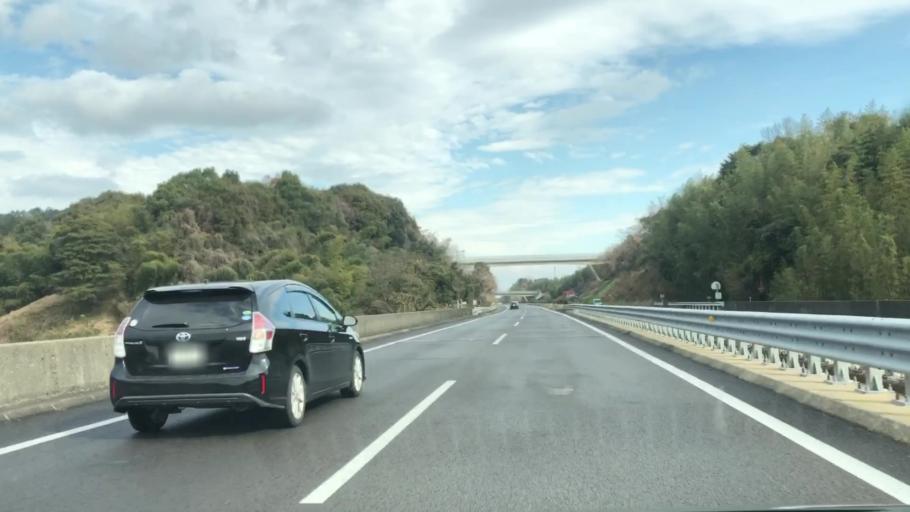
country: JP
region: Saga Prefecture
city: Tosu
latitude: 33.3677
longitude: 130.4584
